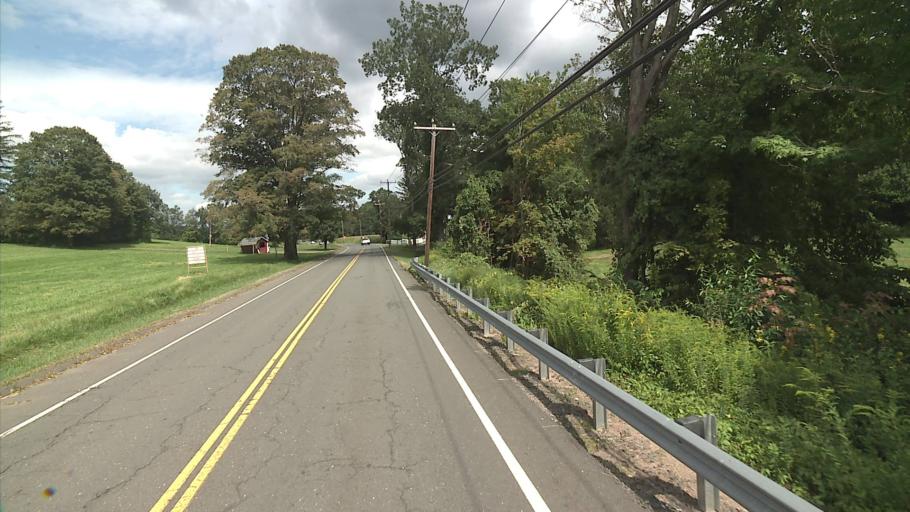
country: US
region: Connecticut
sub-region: Hartford County
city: North Granby
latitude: 41.9888
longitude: -72.8245
